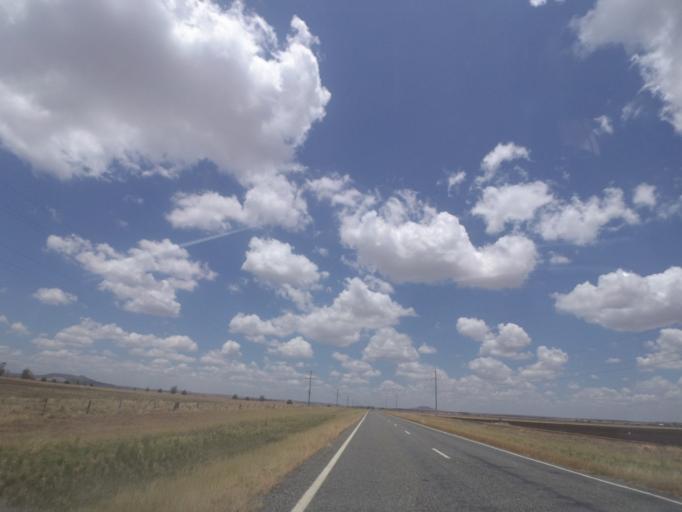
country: AU
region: Queensland
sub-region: Toowoomba
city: Top Camp
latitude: -27.9006
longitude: 151.9762
